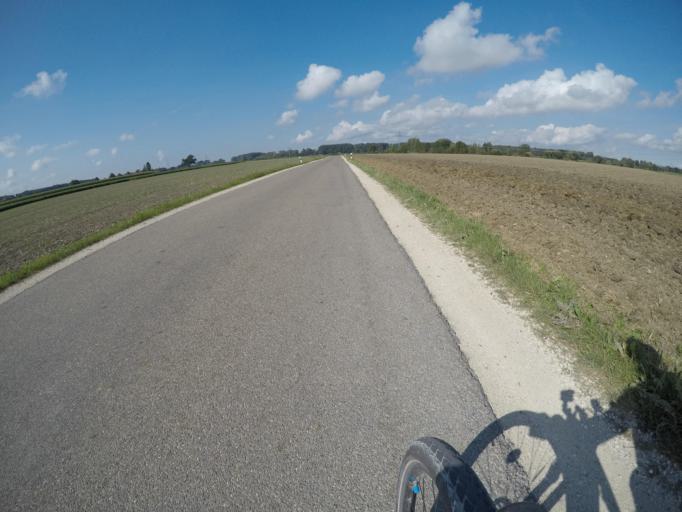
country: DE
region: Bavaria
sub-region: Swabia
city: Tapfheim
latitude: 48.6570
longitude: 10.7217
